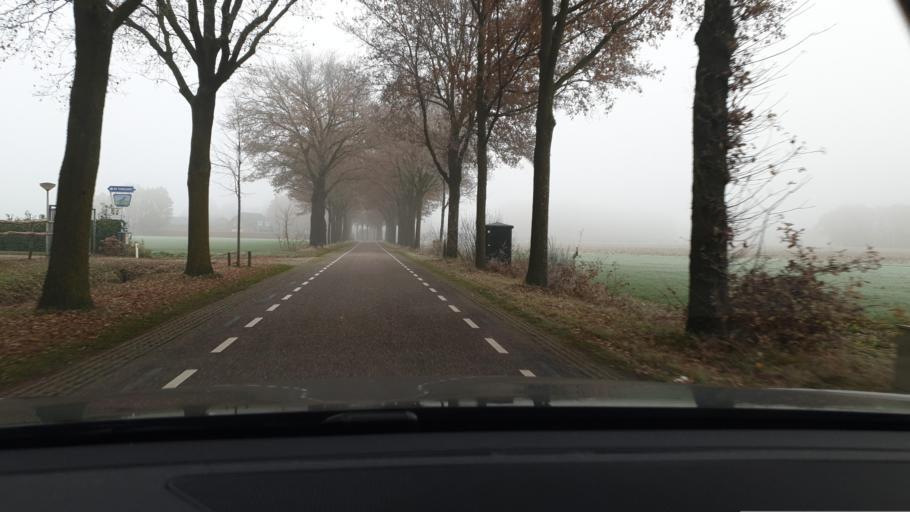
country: NL
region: North Brabant
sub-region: Gemeente Bladel en Netersel
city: Bladel
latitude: 51.3985
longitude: 5.1992
